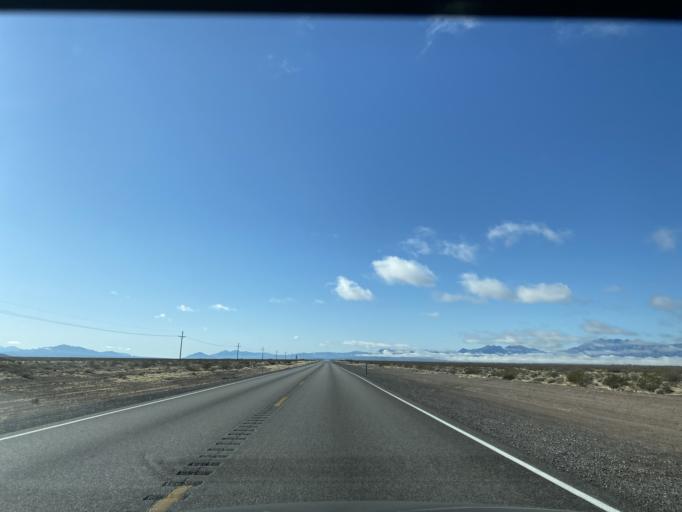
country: US
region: Nevada
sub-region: Nye County
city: Beatty
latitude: 36.6269
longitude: -116.4033
